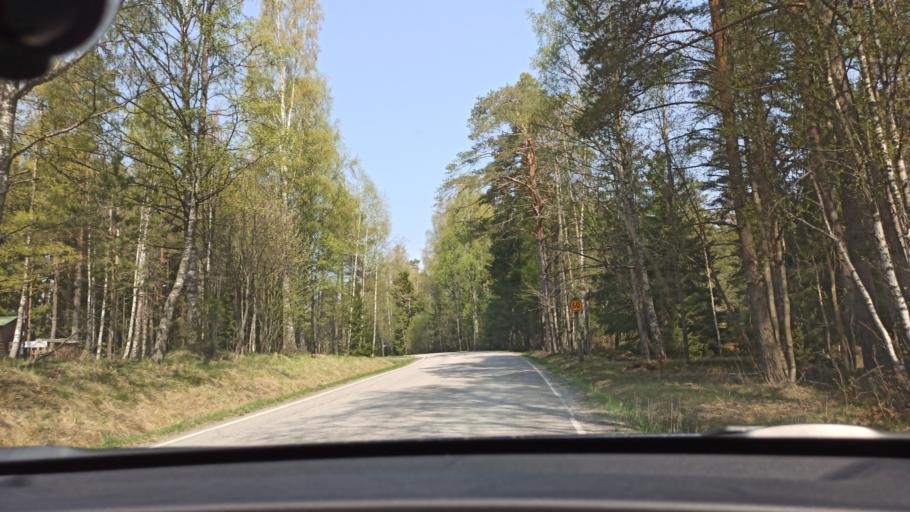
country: FI
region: Uusimaa
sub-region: Helsinki
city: Espoo
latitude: 60.0883
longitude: 24.5885
